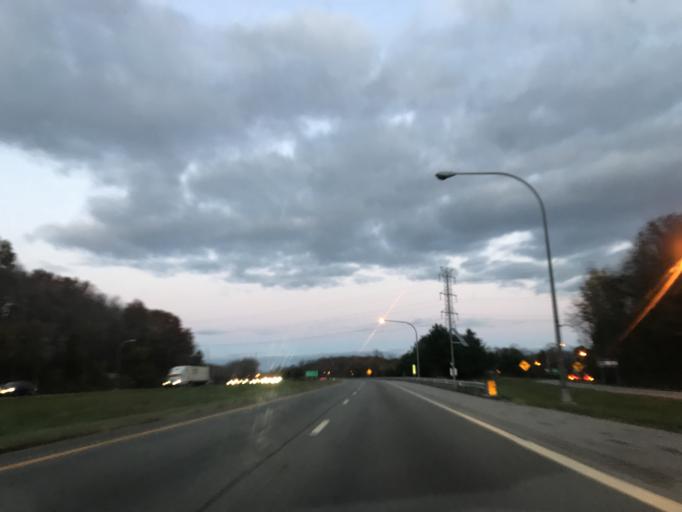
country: US
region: Delaware
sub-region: New Castle County
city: Bellefonte
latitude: 39.7779
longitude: -75.5112
